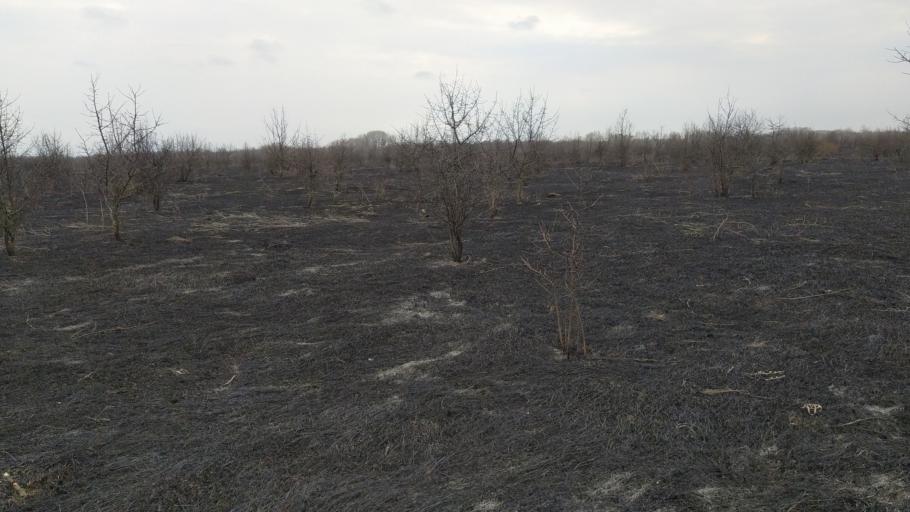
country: RU
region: Rostov
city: Semikarakorsk
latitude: 47.5466
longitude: 40.6831
